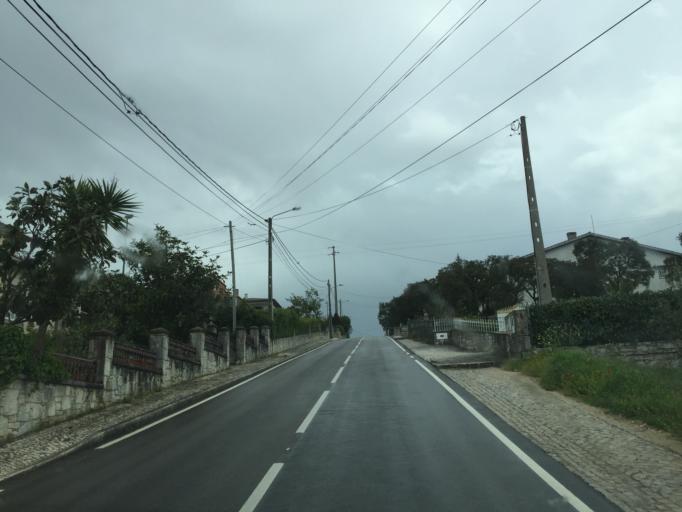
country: PT
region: Santarem
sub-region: Ourem
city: Fatima
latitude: 39.6406
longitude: -8.6816
